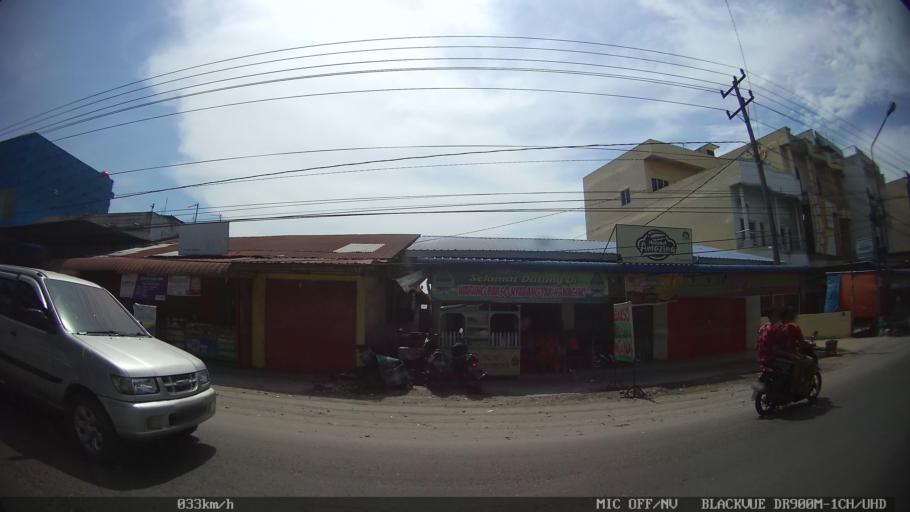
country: ID
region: North Sumatra
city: Labuhan Deli
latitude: 3.6808
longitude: 98.6559
